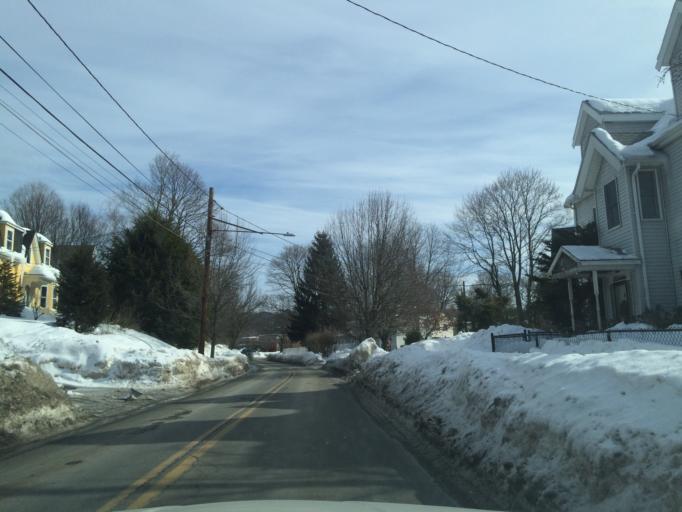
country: US
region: Massachusetts
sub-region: Middlesex County
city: Newton
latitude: 42.3521
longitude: -71.2280
